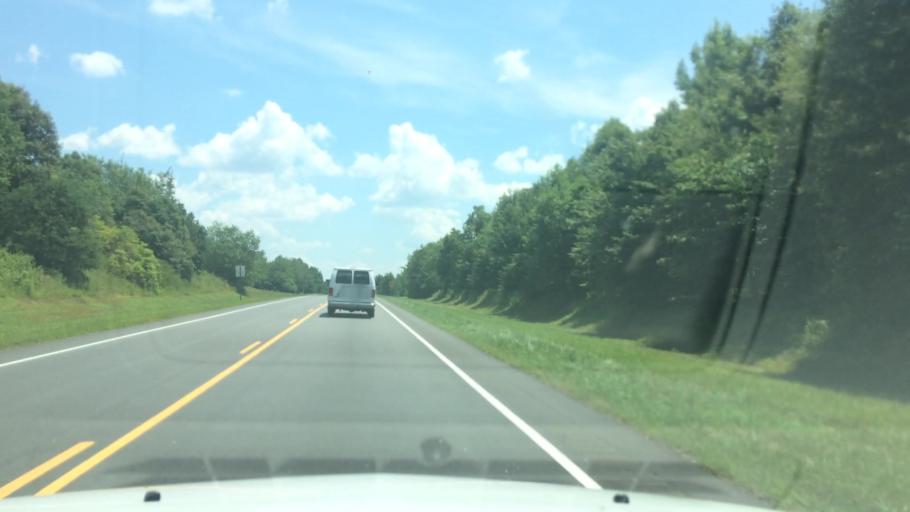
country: US
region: North Carolina
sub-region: Alexander County
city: Stony Point
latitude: 35.8195
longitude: -81.0043
